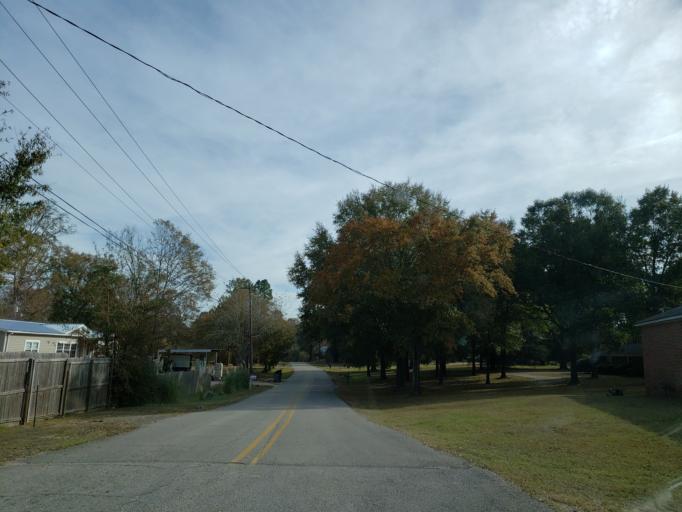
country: US
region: Mississippi
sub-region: Forrest County
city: Rawls Springs
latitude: 31.3805
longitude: -89.3714
